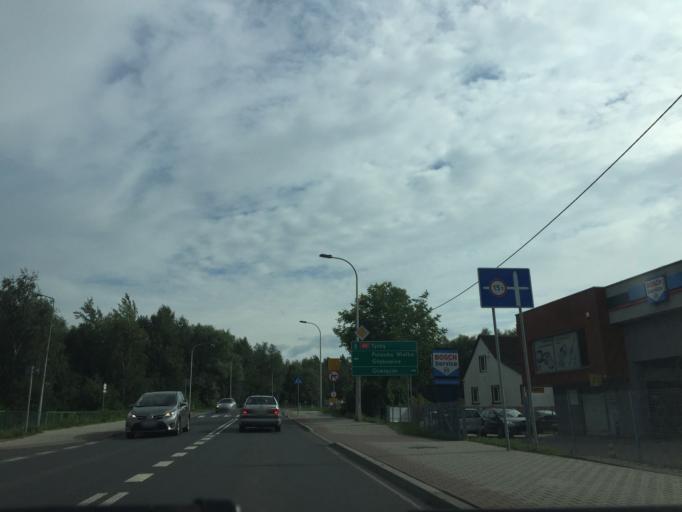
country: PL
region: Lesser Poland Voivodeship
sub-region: Powiat oswiecimski
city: Zaborze
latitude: 50.0254
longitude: 19.2530
